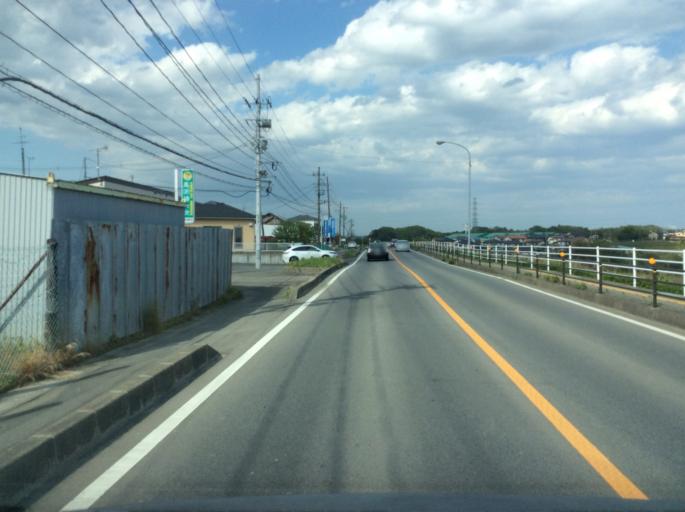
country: JP
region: Fukushima
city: Iwaki
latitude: 36.9288
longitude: 140.8241
